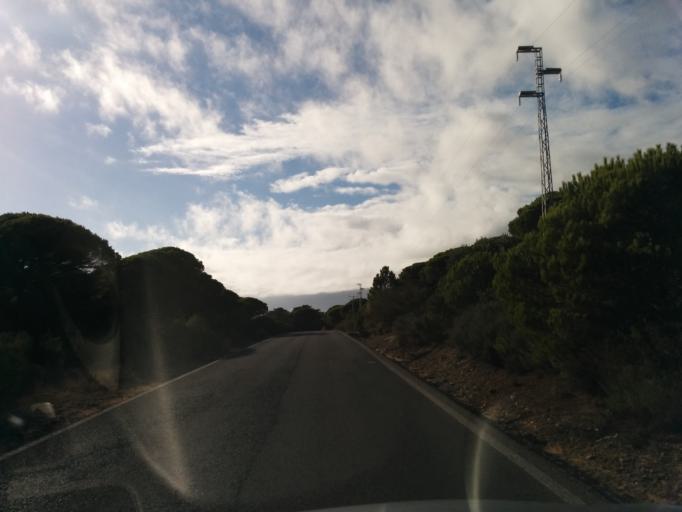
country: ES
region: Andalusia
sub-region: Provincia de Cadiz
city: Vejer de la Frontera
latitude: 36.1933
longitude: -5.9903
